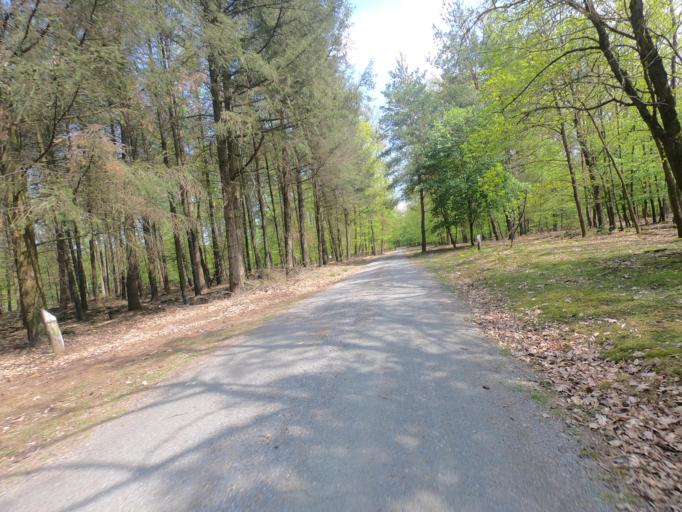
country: DE
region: Hesse
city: Niederrad
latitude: 50.0521
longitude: 8.6304
